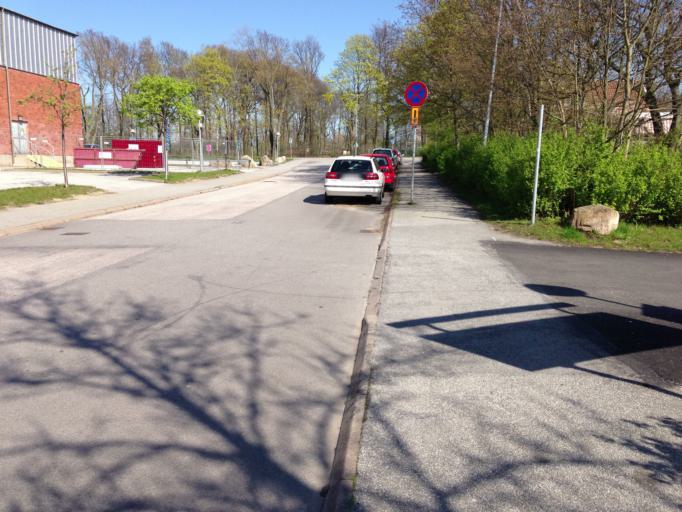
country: SE
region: Skane
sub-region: Lunds Kommun
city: Lund
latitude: 55.7180
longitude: 13.2008
